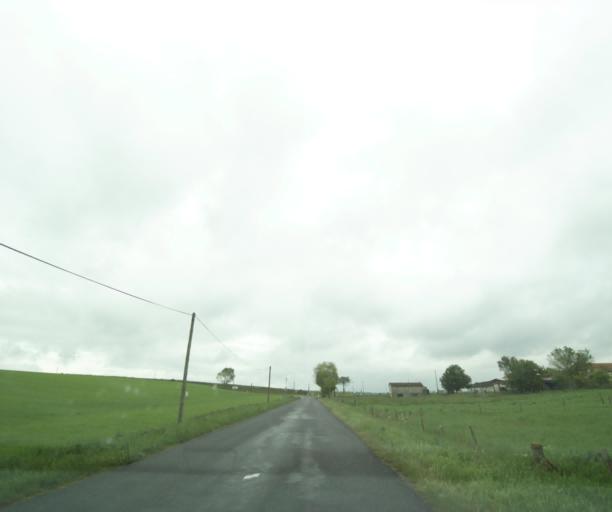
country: FR
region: Poitou-Charentes
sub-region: Departement de la Charente-Maritime
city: Perignac
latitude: 45.6483
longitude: -0.5275
